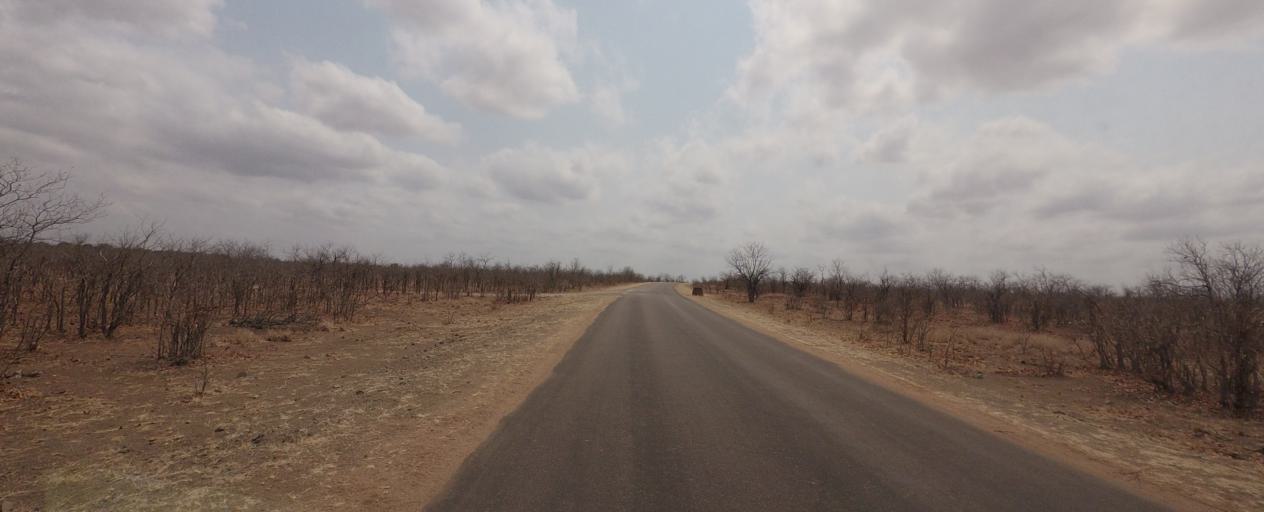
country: ZA
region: Limpopo
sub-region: Mopani District Municipality
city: Phalaborwa
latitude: -23.5839
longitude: 31.4502
